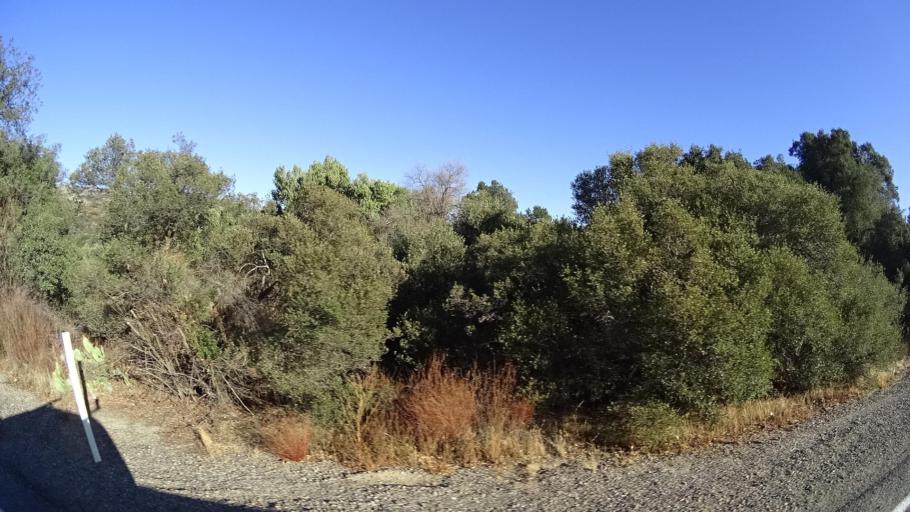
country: US
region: California
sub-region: San Diego County
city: Campo
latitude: 32.6046
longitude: -116.4863
